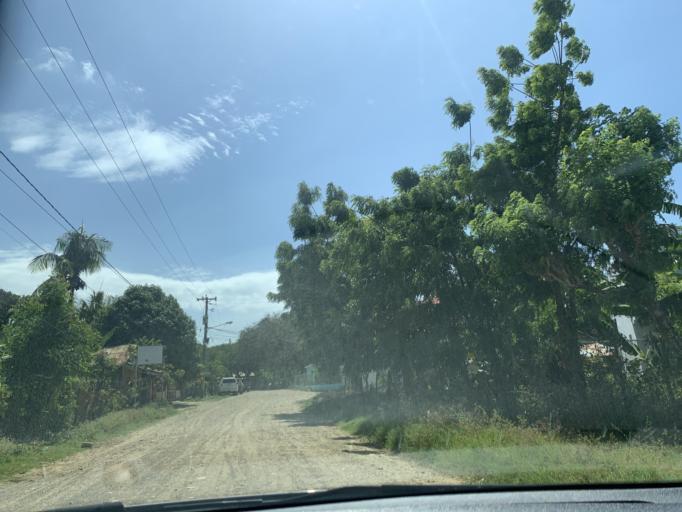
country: DO
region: Puerto Plata
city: Luperon
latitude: 19.8902
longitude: -70.8844
